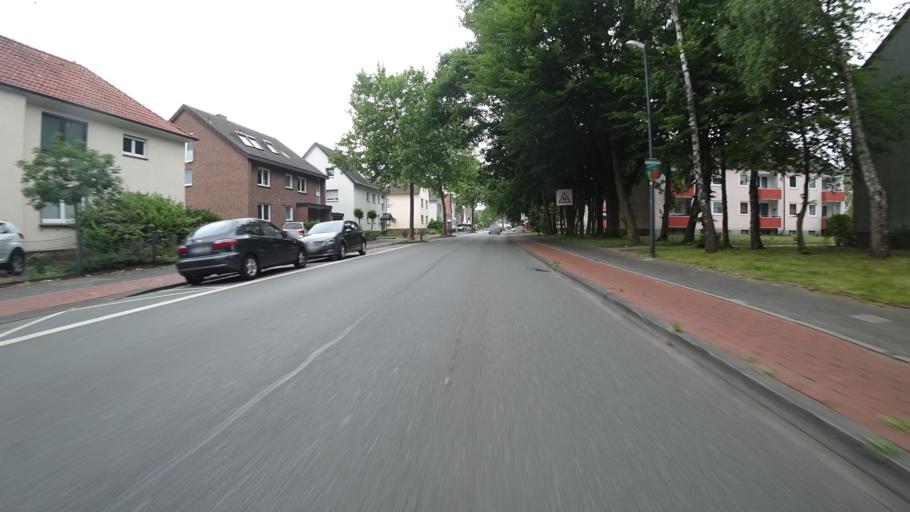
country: DE
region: North Rhine-Westphalia
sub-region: Regierungsbezirk Detmold
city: Guetersloh
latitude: 51.9262
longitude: 8.3848
